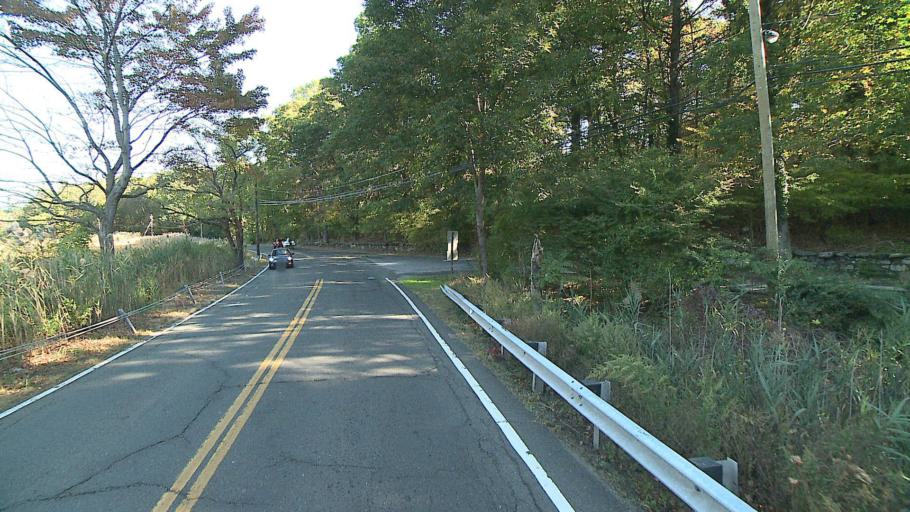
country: US
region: Connecticut
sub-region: Fairfield County
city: Darien
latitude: 41.0725
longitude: -73.4284
